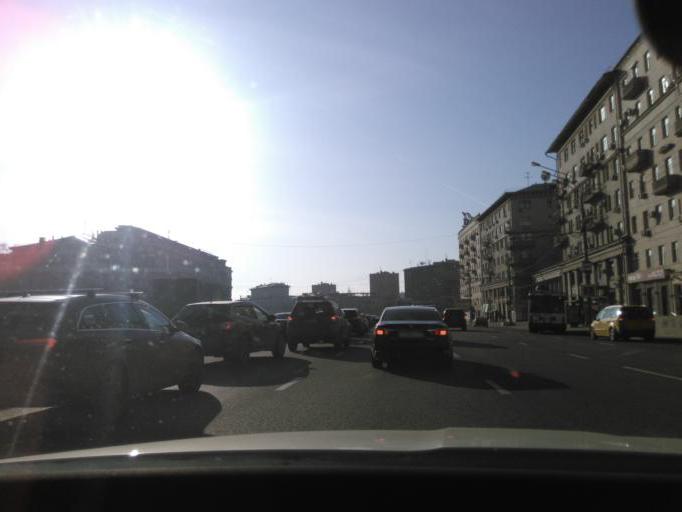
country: RU
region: Moskovskaya
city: Dorogomilovo
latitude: 55.7408
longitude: 37.5846
